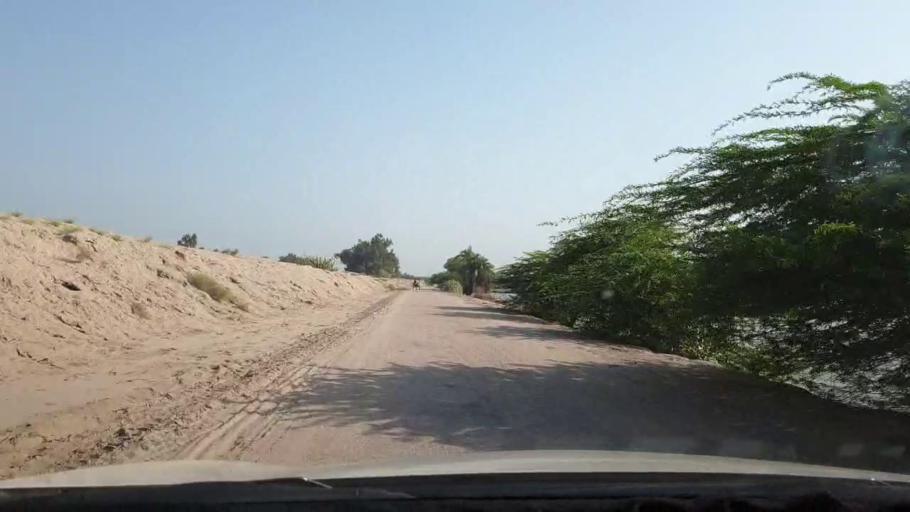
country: PK
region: Sindh
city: Larkana
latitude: 27.5465
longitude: 68.2555
